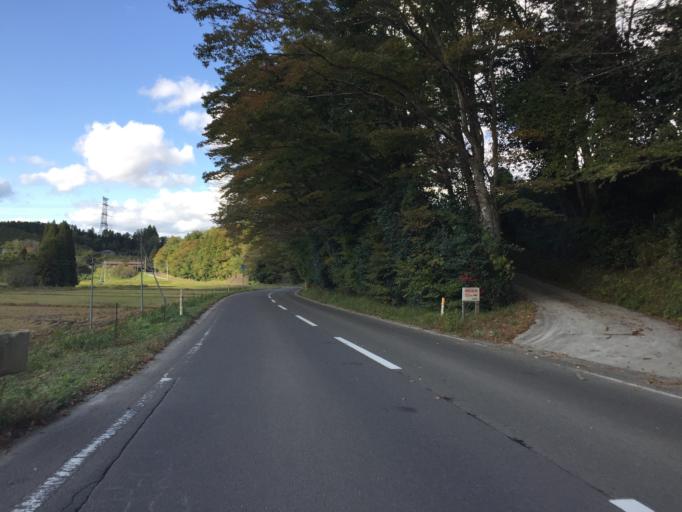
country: JP
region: Miyagi
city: Marumori
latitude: 37.8516
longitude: 140.8321
